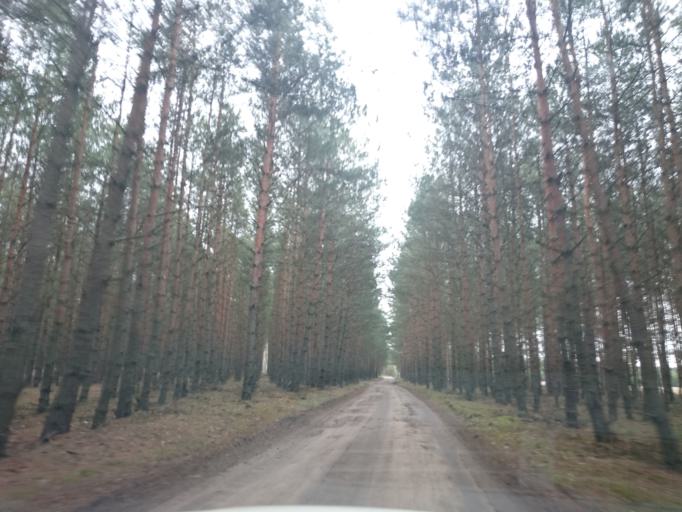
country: PL
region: Kujawsko-Pomorskie
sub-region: Powiat golubsko-dobrzynski
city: Ciechocin
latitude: 53.0502
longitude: 18.8561
